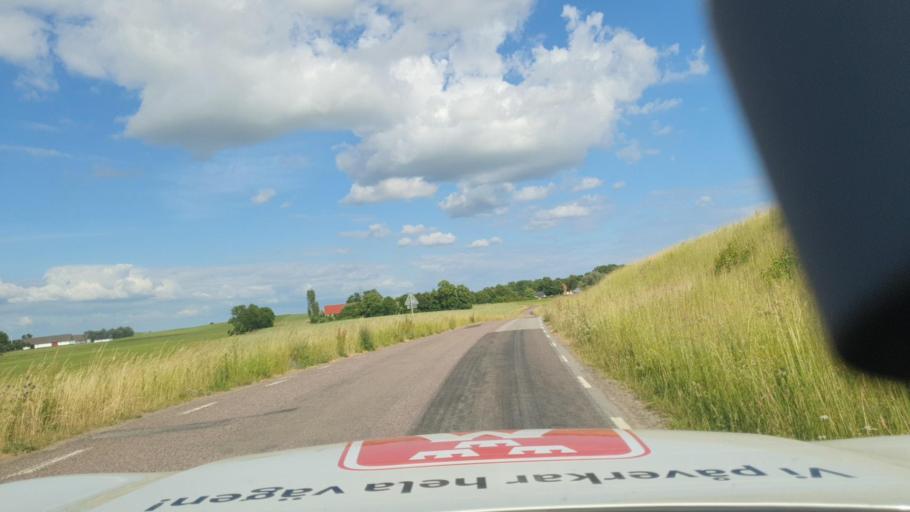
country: SE
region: Skane
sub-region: Skurups Kommun
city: Skurup
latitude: 55.4536
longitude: 13.5362
